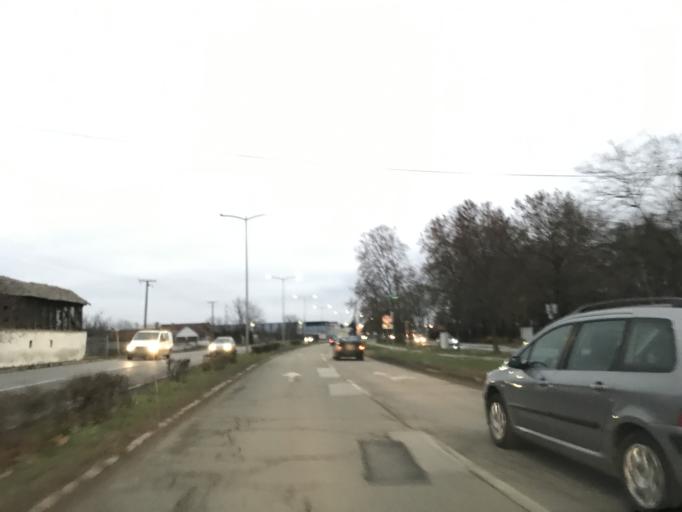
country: RS
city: Veternik
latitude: 45.2791
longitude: 19.7922
